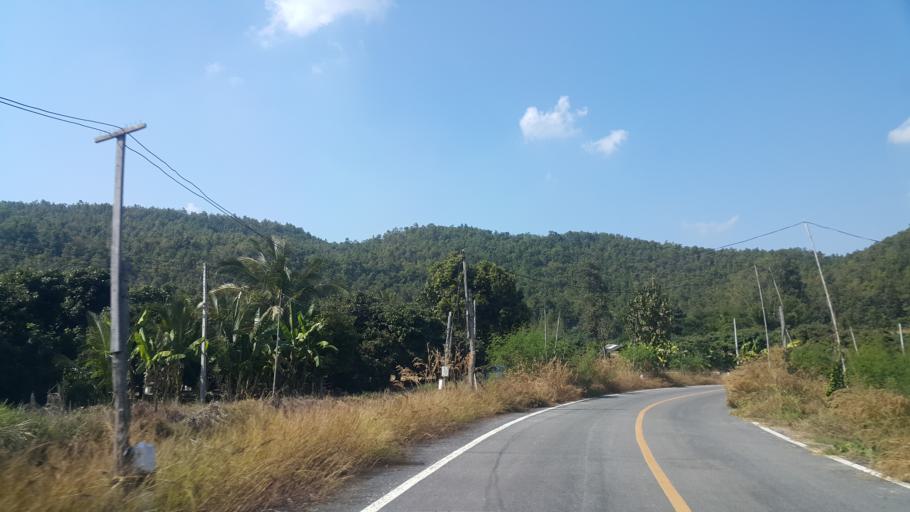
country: TH
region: Lamphun
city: Ban Thi
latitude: 18.6224
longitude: 99.1492
